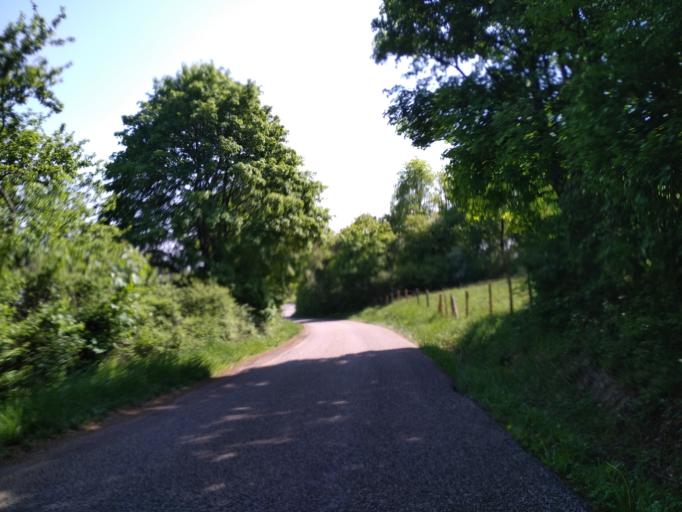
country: FR
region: Rhone-Alpes
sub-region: Departement du Rhone
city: Limonest
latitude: 45.8388
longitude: 4.7989
